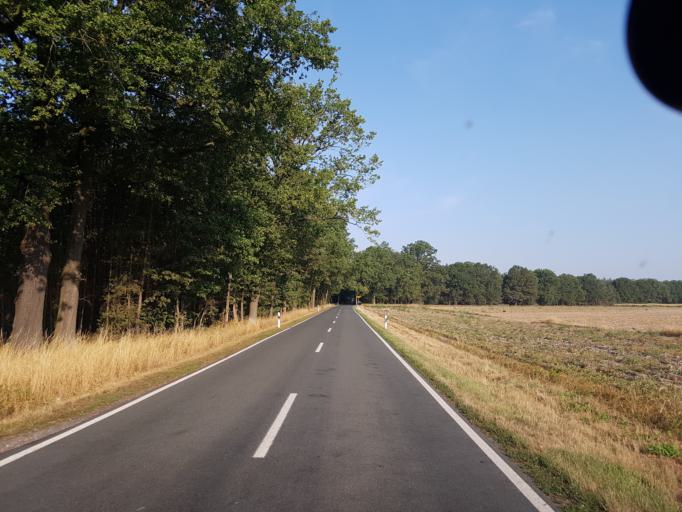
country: DE
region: Brandenburg
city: Finsterwalde
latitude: 51.6785
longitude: 13.6954
